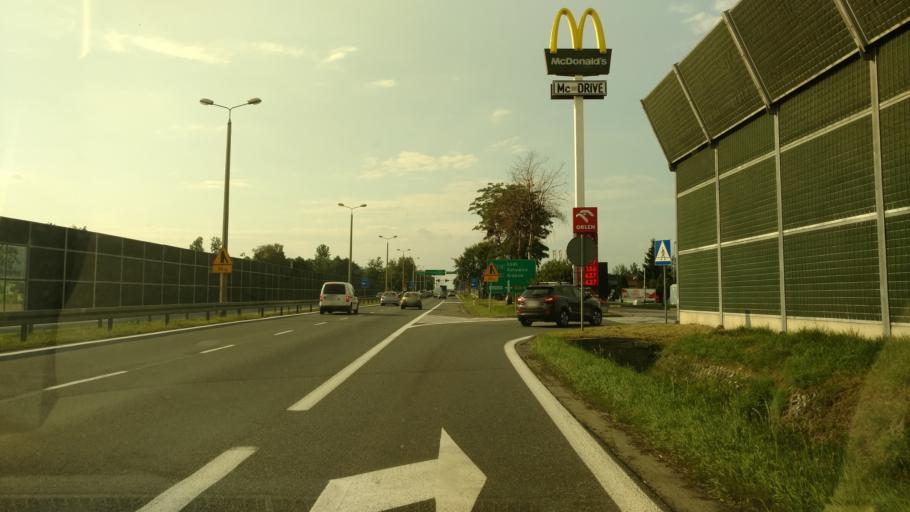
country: PL
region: Silesian Voivodeship
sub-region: Powiat pszczynski
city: Pszczyna
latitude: 49.9865
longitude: 18.9553
